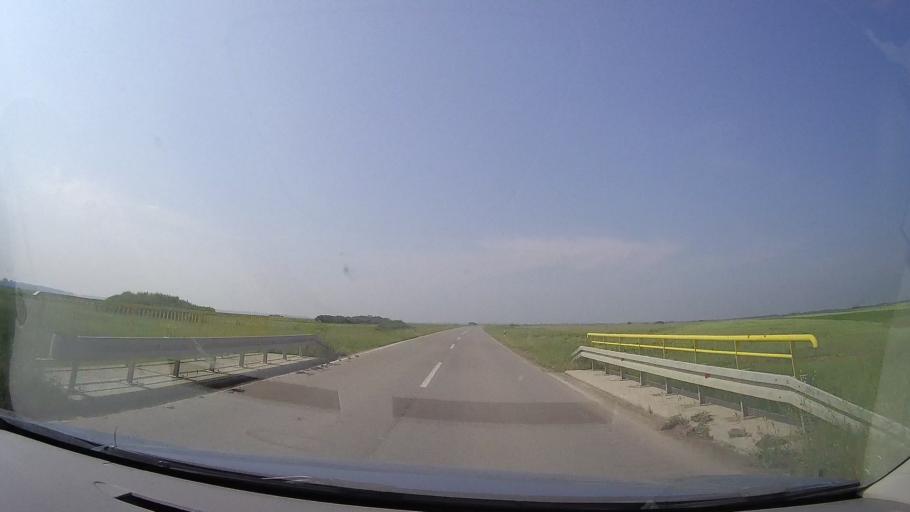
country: RS
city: Jasa Tomic
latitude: 45.4212
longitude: 20.8355
